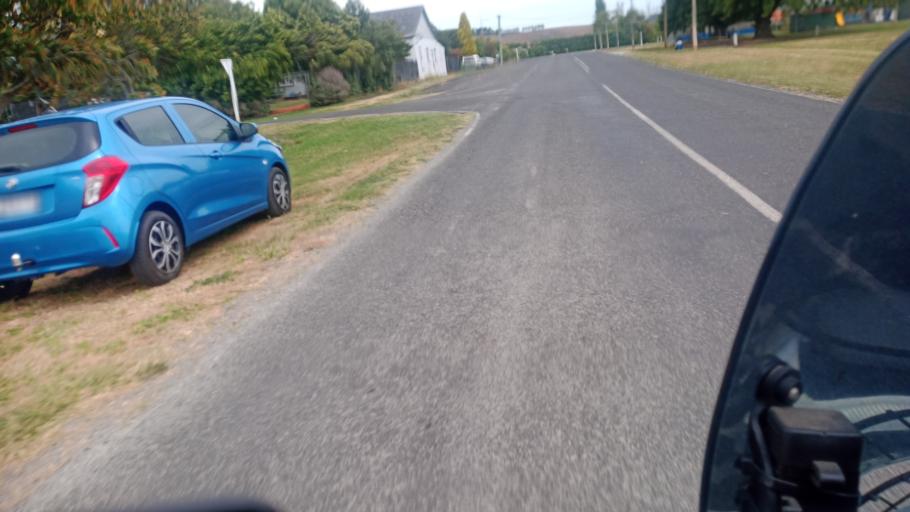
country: NZ
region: Gisborne
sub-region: Gisborne District
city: Gisborne
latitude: -38.6235
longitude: 177.8901
